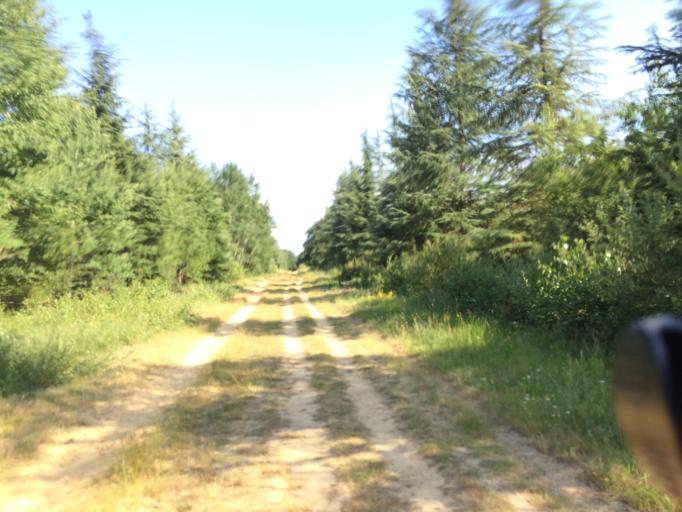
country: FR
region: Ile-de-France
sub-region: Departement de l'Essonne
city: Montgeron
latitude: 48.6771
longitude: 2.4502
